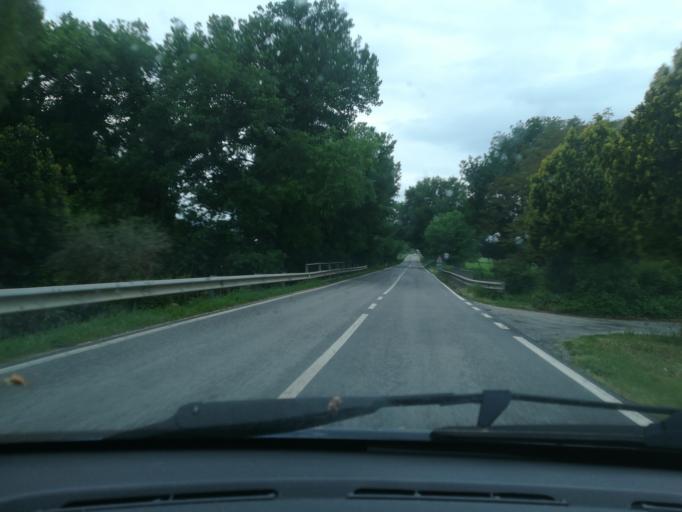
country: IT
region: The Marches
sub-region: Provincia di Macerata
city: Treia
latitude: 43.2721
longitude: 13.2818
